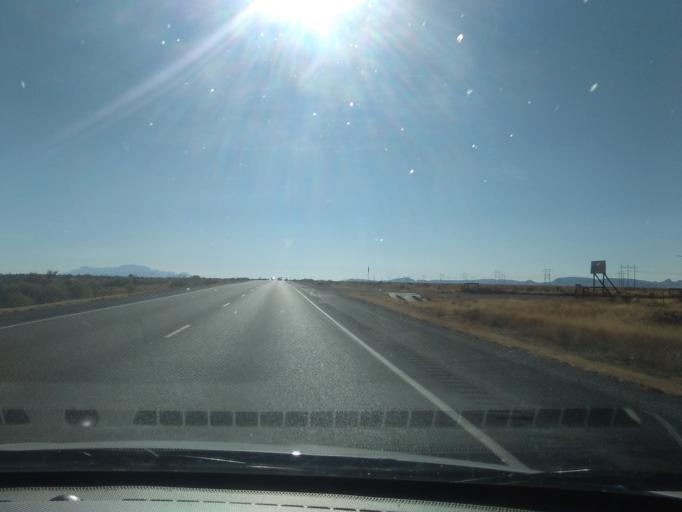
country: US
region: New Mexico
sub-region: Dona Ana County
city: Hatch
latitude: 32.5373
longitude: -107.4853
